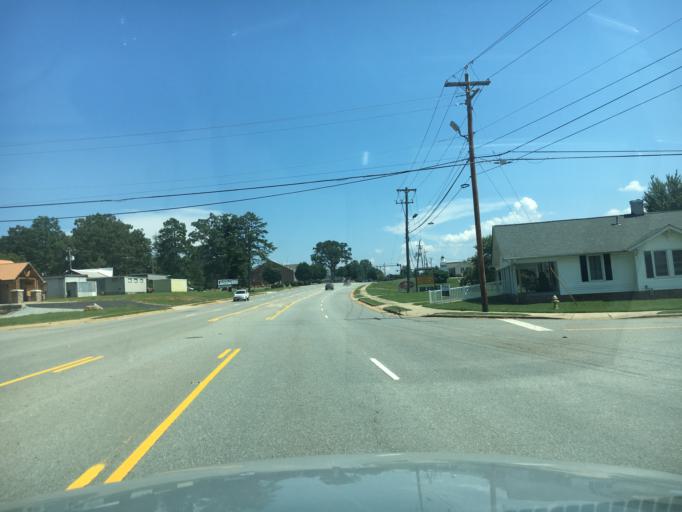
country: US
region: North Carolina
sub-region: Rutherford County
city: Forest City
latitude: 35.3328
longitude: -81.8729
